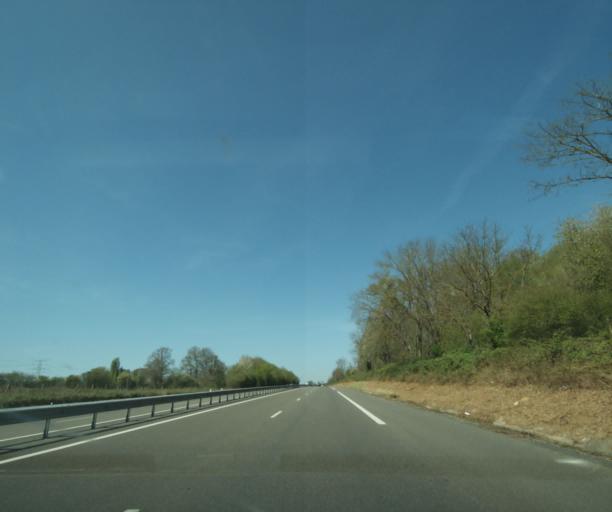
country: FR
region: Bourgogne
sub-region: Departement de la Nievre
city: Coulanges-les-Nevers
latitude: 47.0203
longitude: 3.1936
